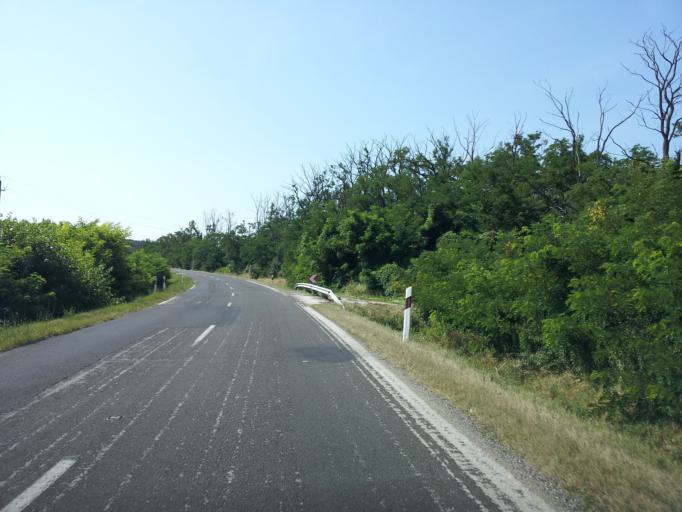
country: HU
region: Fejer
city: Lovasbereny
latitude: 47.2762
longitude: 18.5252
